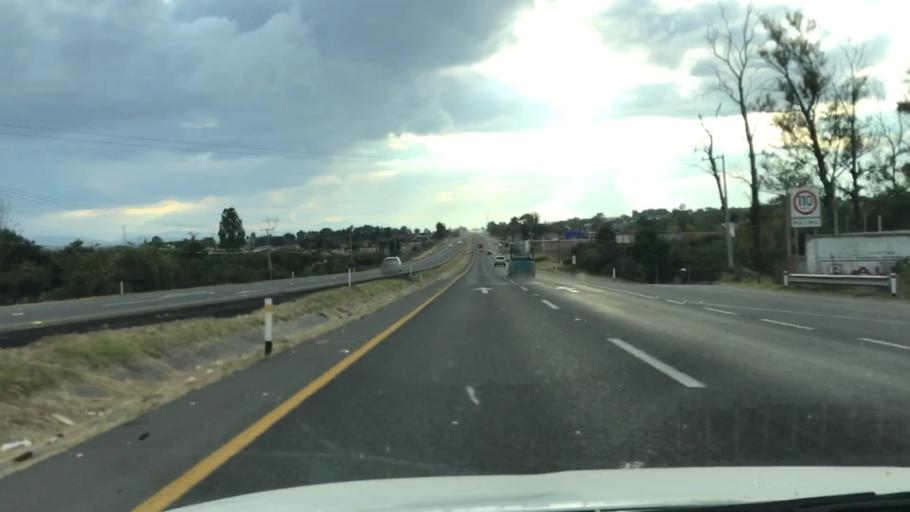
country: MX
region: Guanajuato
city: Penjamo
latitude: 20.4084
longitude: -101.7392
